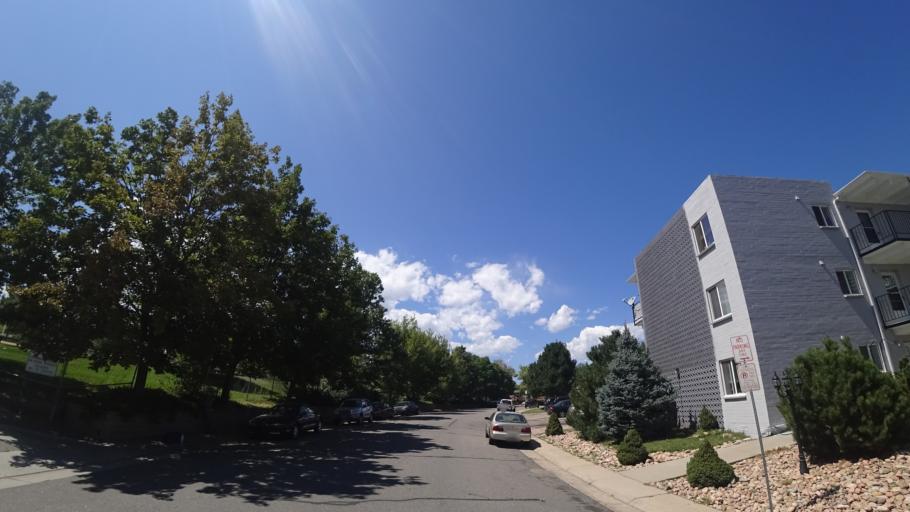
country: US
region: Colorado
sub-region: Arapahoe County
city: Littleton
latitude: 39.6107
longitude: -104.9901
